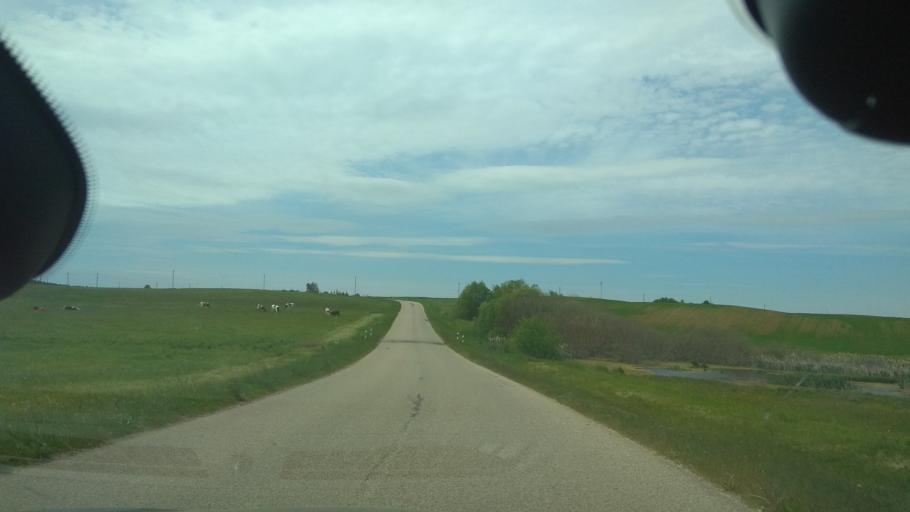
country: LT
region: Vilnius County
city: Ukmerge
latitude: 55.1616
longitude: 24.5372
